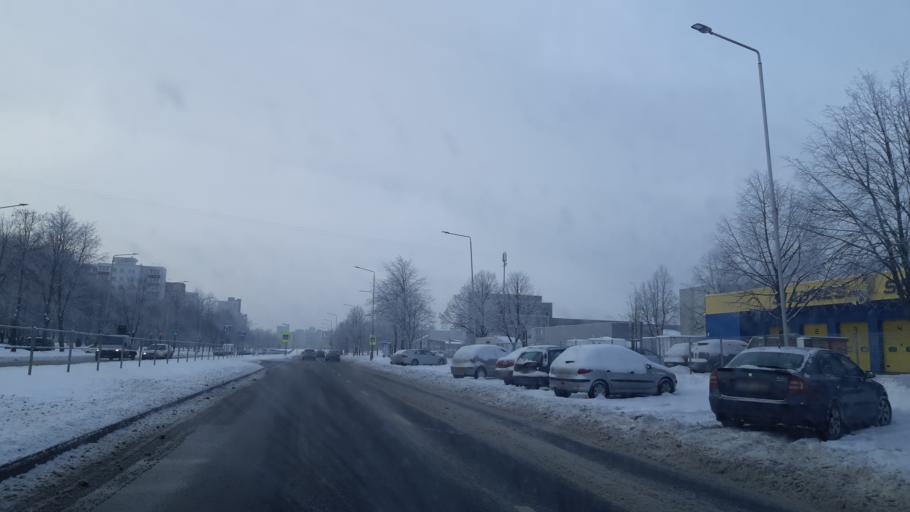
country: LT
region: Kauno apskritis
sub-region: Kaunas
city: Eiguliai
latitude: 54.9313
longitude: 23.9505
